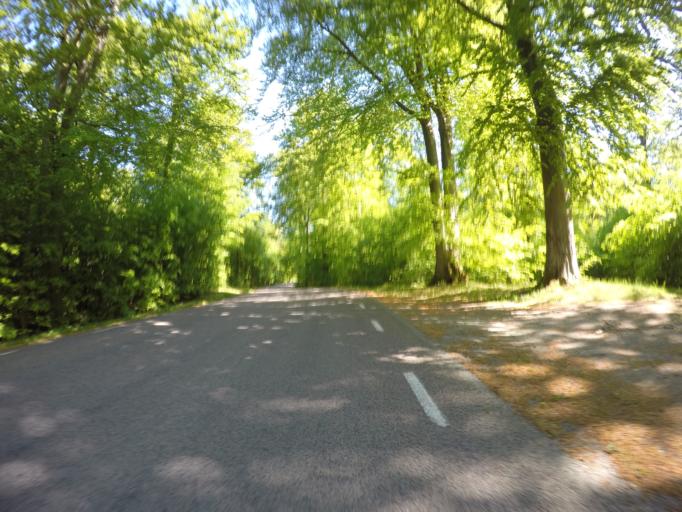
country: SE
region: Skane
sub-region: Svedala Kommun
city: Klagerup
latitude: 55.5548
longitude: 13.2098
